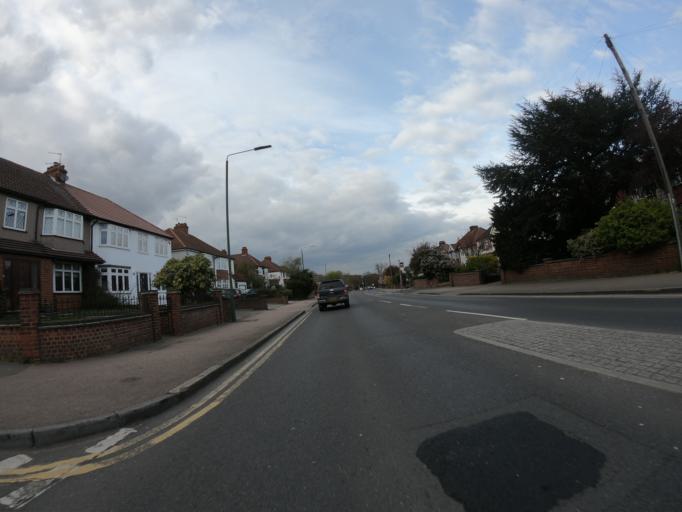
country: GB
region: England
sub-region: Greater London
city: Bexleyheath
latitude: 51.4631
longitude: 0.1541
